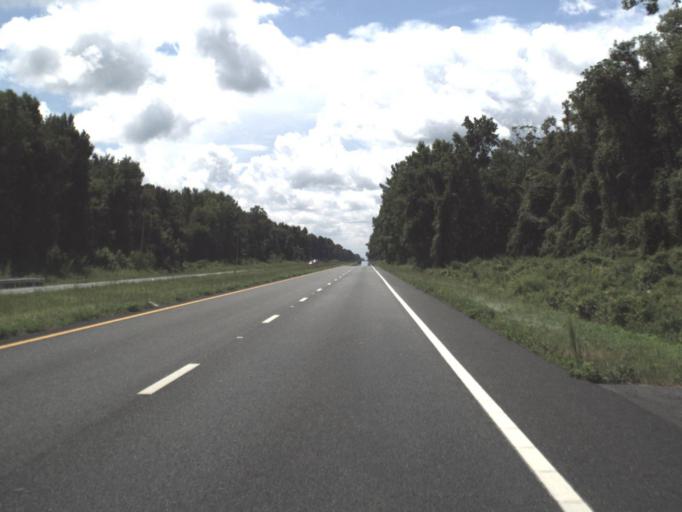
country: US
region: Florida
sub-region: Taylor County
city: Perry
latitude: 30.3101
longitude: -83.7545
